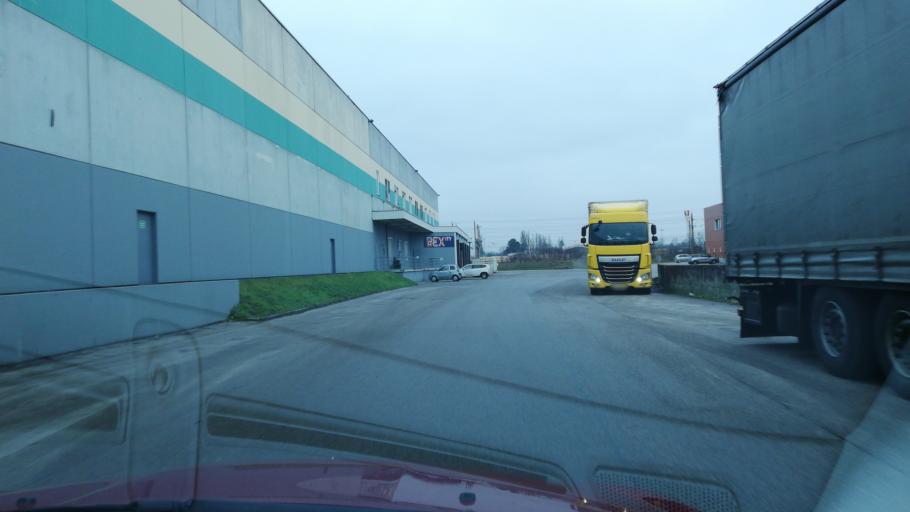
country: AT
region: Upper Austria
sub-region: Wels Stadt
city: Wels
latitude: 48.1796
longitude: 14.0613
